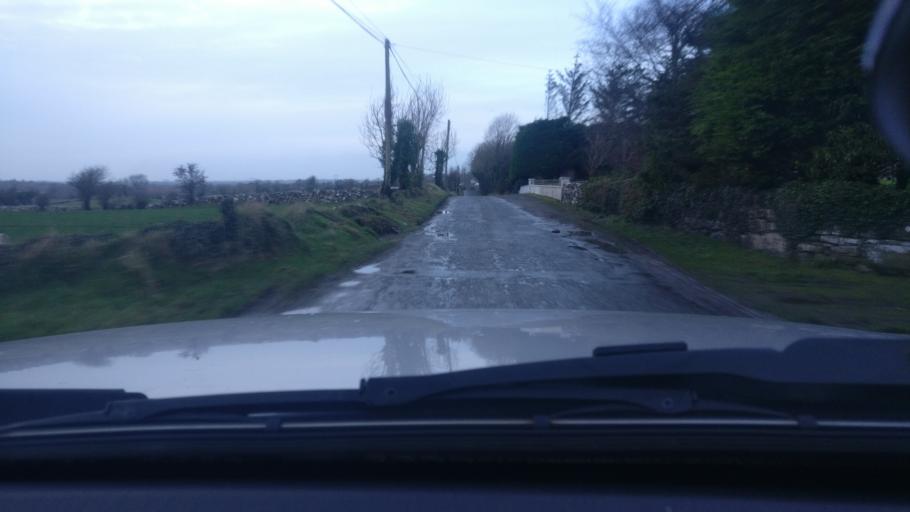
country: IE
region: Connaught
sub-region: County Galway
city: Loughrea
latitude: 53.1767
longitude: -8.5883
